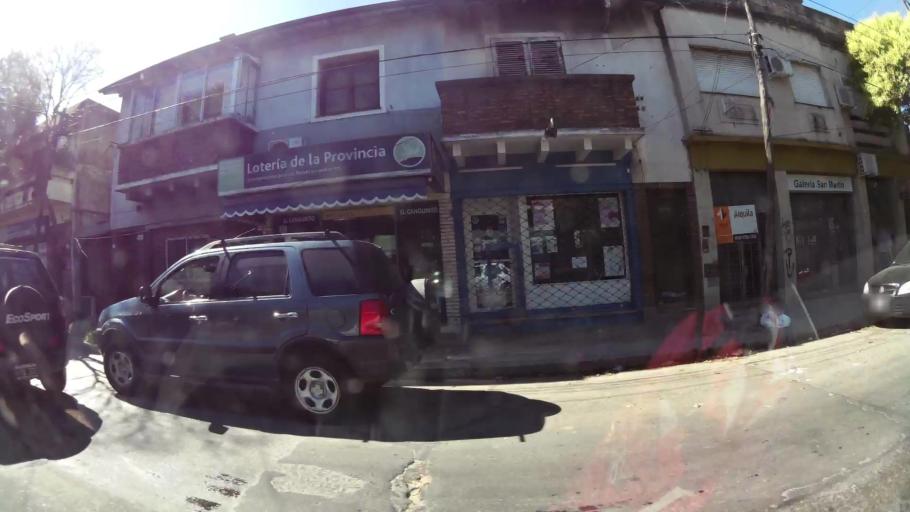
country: AR
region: Buenos Aires
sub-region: Partido de General San Martin
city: General San Martin
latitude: -34.5379
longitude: -58.5123
